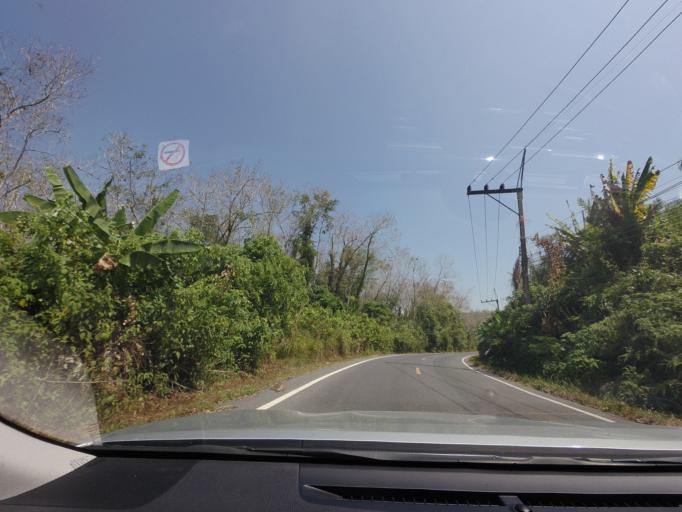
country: TH
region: Phangnga
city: Takua Thung
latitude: 8.2527
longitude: 98.4024
